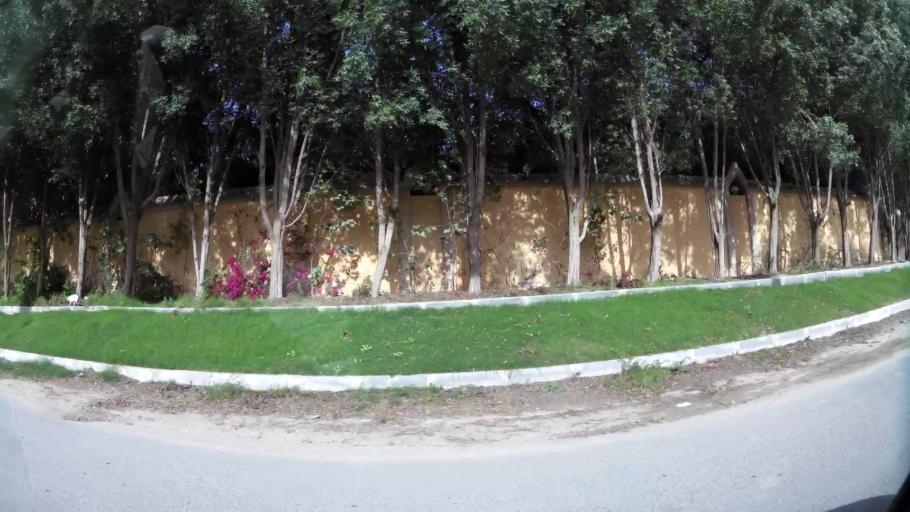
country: QA
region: Baladiyat ar Rayyan
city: Ar Rayyan
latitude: 25.3464
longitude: 51.4264
